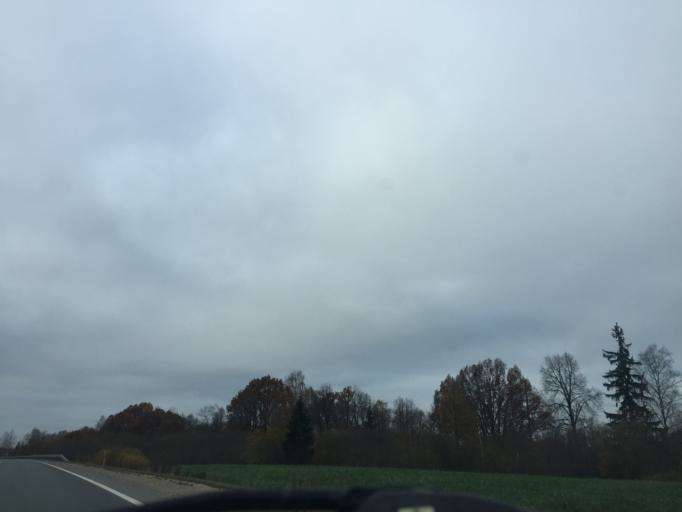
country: LV
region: Saldus Rajons
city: Saldus
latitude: 56.6722
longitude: 22.3821
